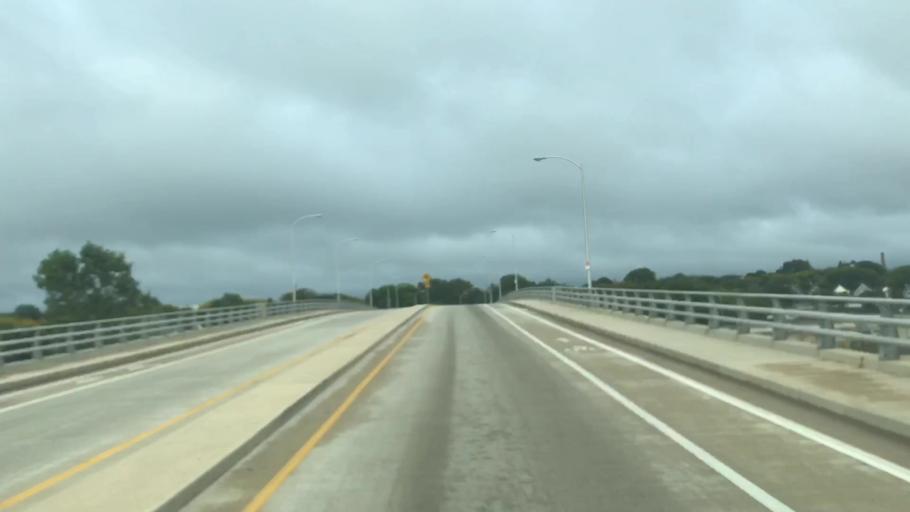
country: US
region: Wisconsin
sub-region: Milwaukee County
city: Milwaukee
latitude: 43.0038
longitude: -87.8940
